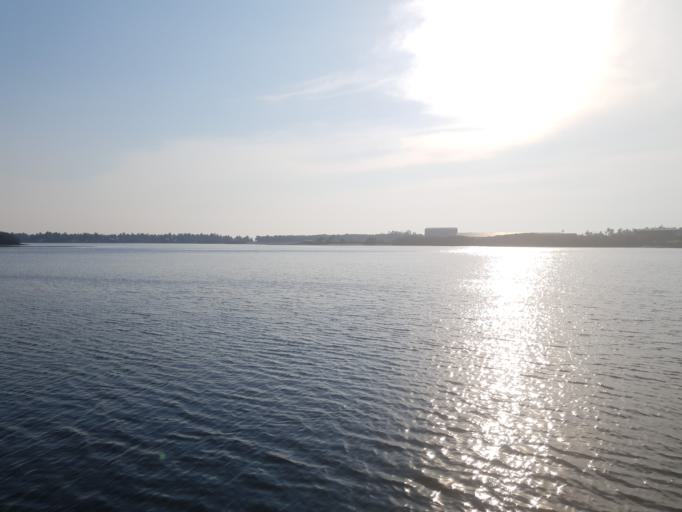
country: IN
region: Karnataka
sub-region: Dakshina Kannada
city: Mangalore
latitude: 12.8740
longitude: 74.8280
